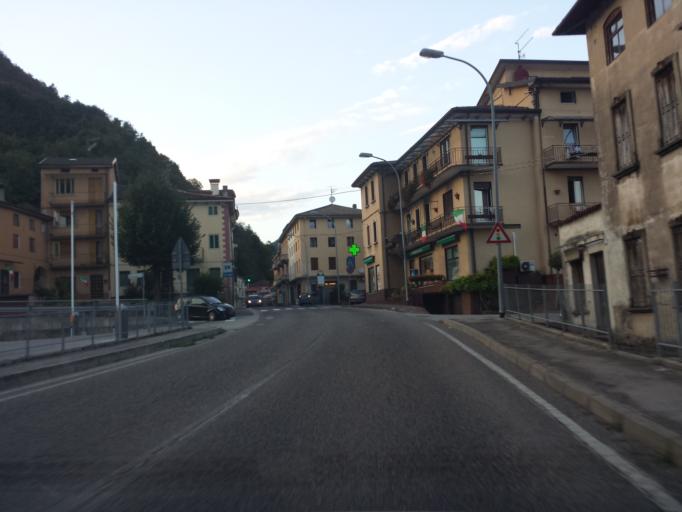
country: IT
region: Veneto
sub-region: Provincia di Vicenza
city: San Quirico
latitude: 45.6752
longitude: 11.2711
